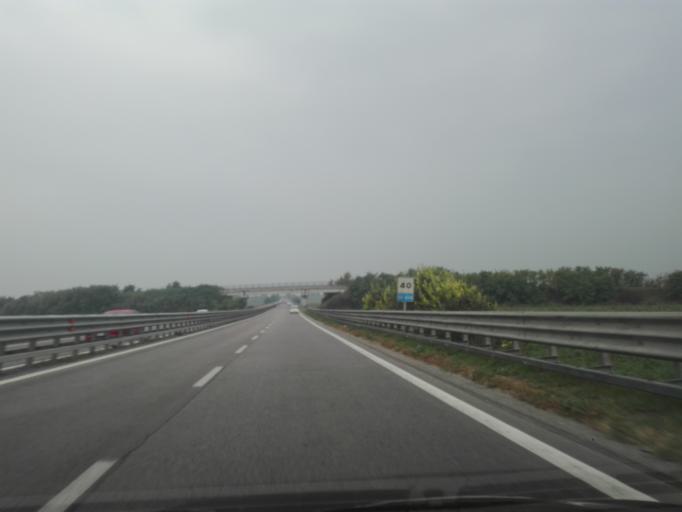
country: IT
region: Veneto
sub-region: Provincia di Verona
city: Legnago
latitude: 45.1677
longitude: 11.2978
